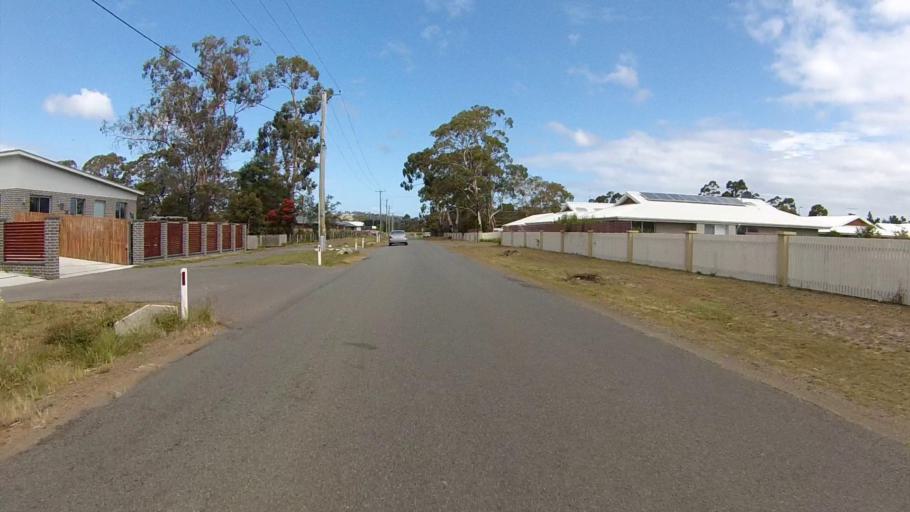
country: AU
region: Tasmania
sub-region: Clarence
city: Lauderdale
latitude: -42.9054
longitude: 147.4856
